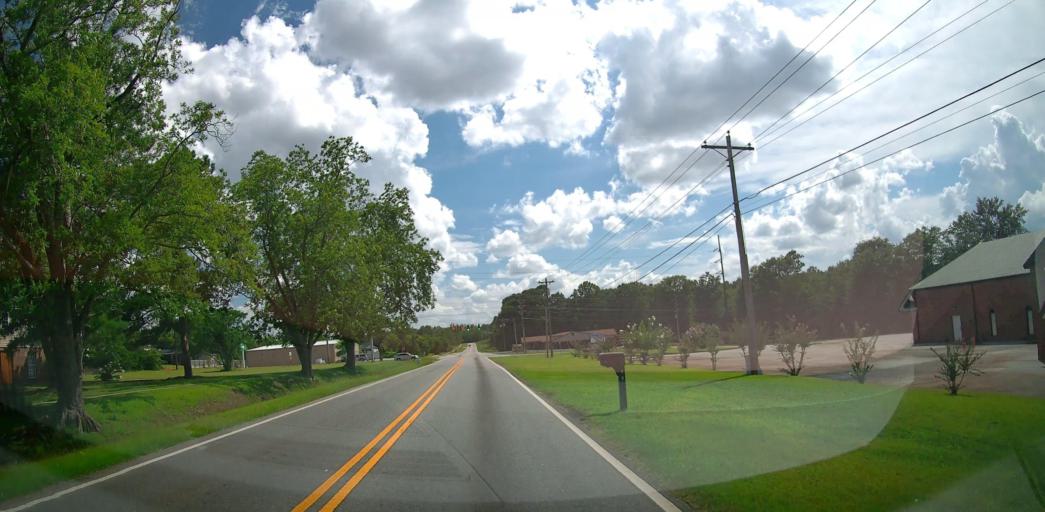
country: US
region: Georgia
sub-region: Houston County
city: Warner Robins
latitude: 32.6517
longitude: -83.6256
